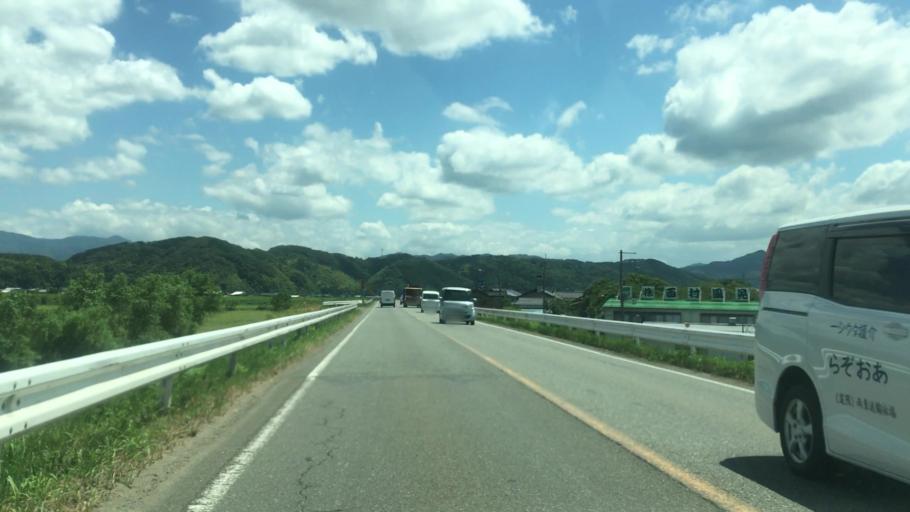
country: JP
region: Hyogo
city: Toyooka
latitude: 35.5149
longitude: 134.8210
